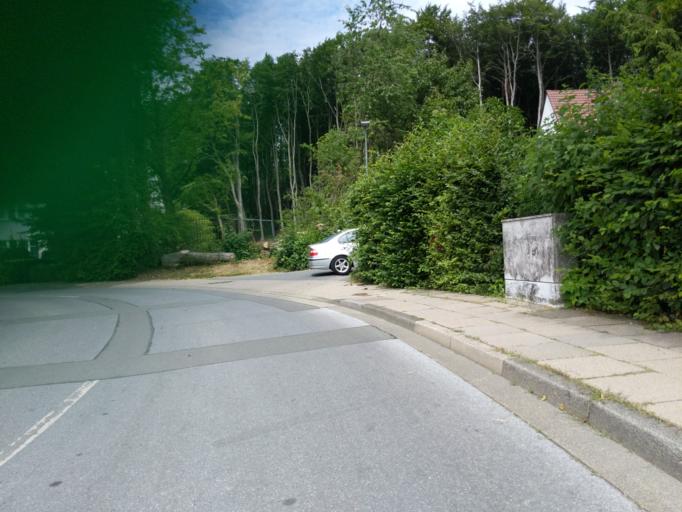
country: DE
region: North Rhine-Westphalia
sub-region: Regierungsbezirk Detmold
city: Bielefeld
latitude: 52.0273
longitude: 8.4797
